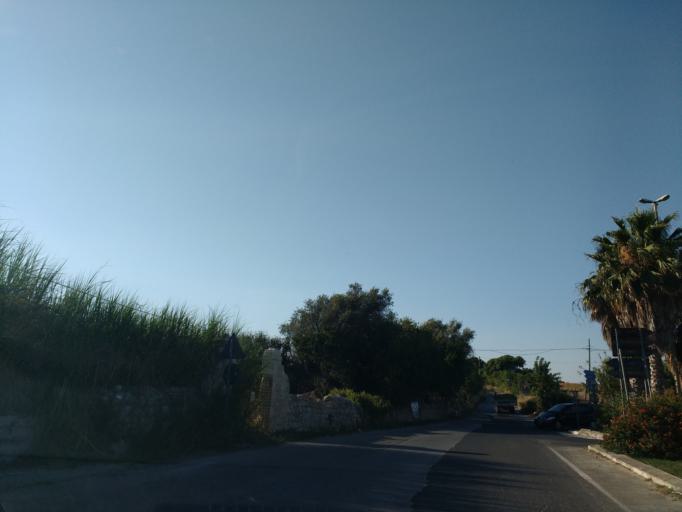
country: IT
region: Sicily
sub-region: Ragusa
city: Pozzallo
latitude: 36.7313
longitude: 14.8957
